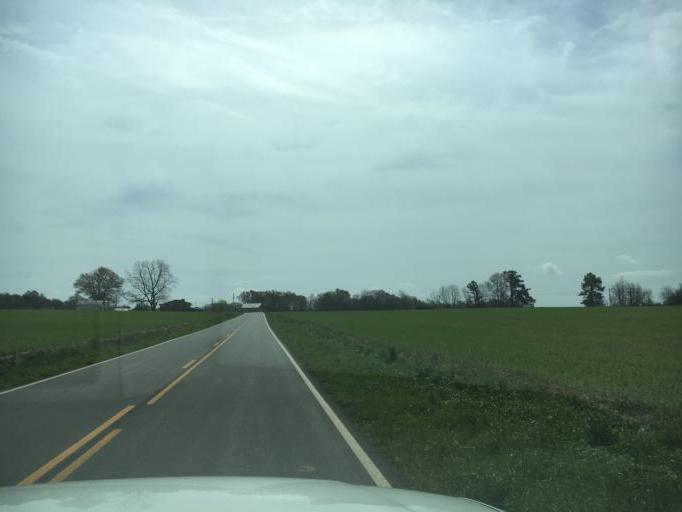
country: US
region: Georgia
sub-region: Franklin County
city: Lavonia
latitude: 34.4014
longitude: -83.0765
